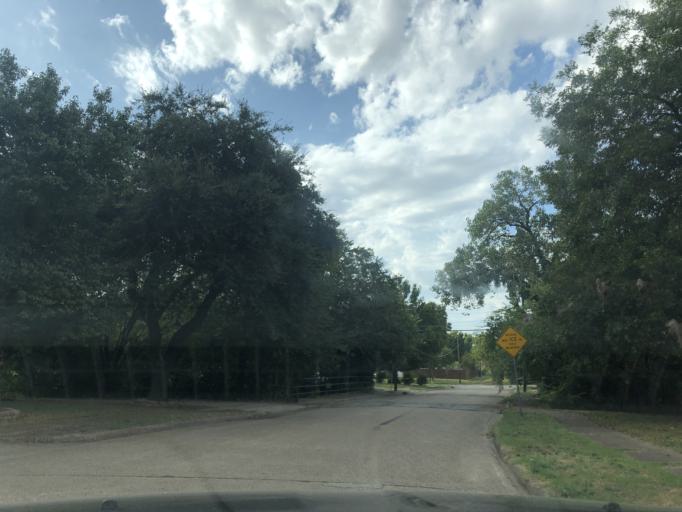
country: US
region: Texas
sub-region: Dallas County
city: Garland
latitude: 32.8870
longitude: -96.6621
